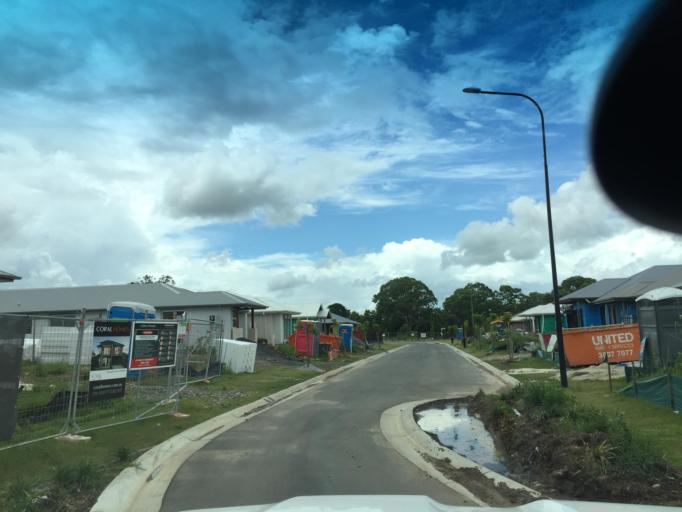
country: AU
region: Queensland
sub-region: Moreton Bay
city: Caboolture South
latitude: -27.0935
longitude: 152.9653
